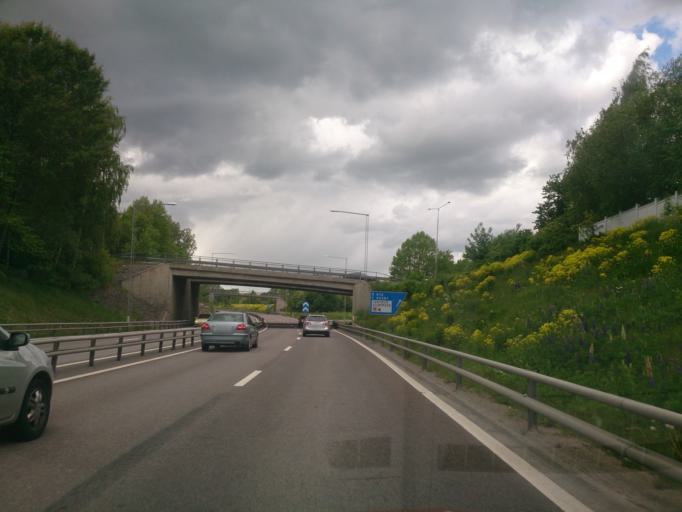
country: SE
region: OEstergoetland
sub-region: Norrkopings Kommun
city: Norrkoping
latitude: 58.5747
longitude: 16.1810
